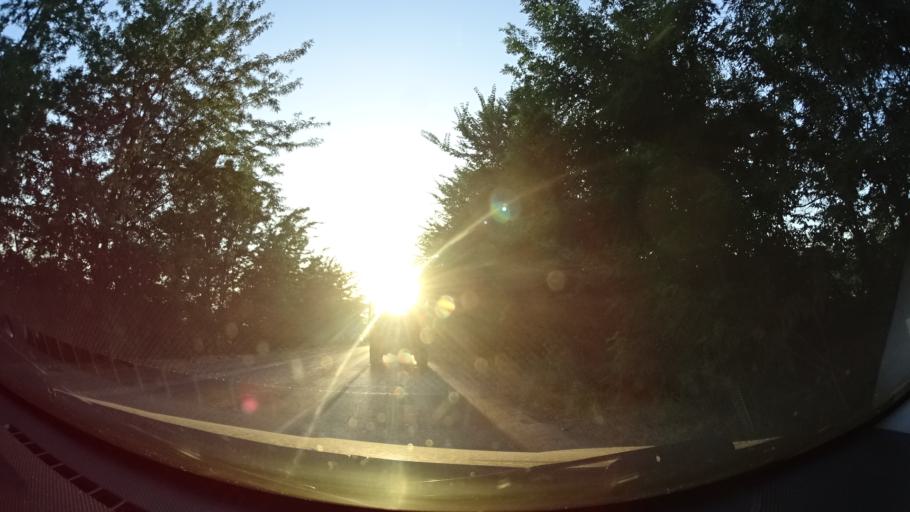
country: GE
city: Bagdadi
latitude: 41.8513
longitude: 46.0418
